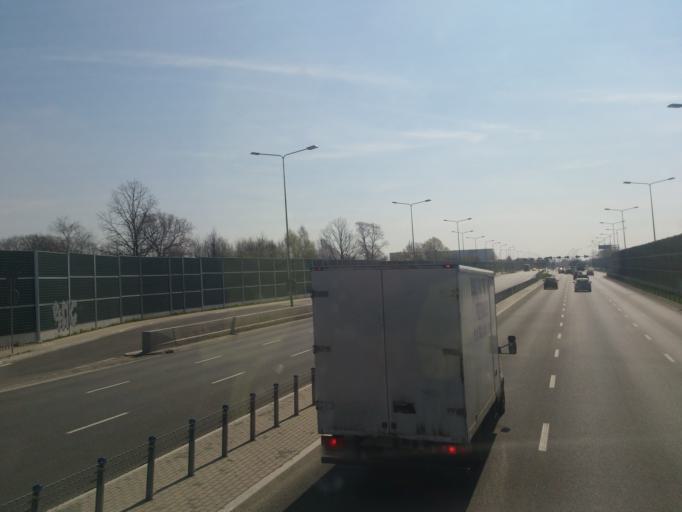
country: PL
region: Lodz Voivodeship
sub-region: Powiat lodzki wschodni
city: Starowa Gora
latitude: 51.7083
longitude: 19.4646
